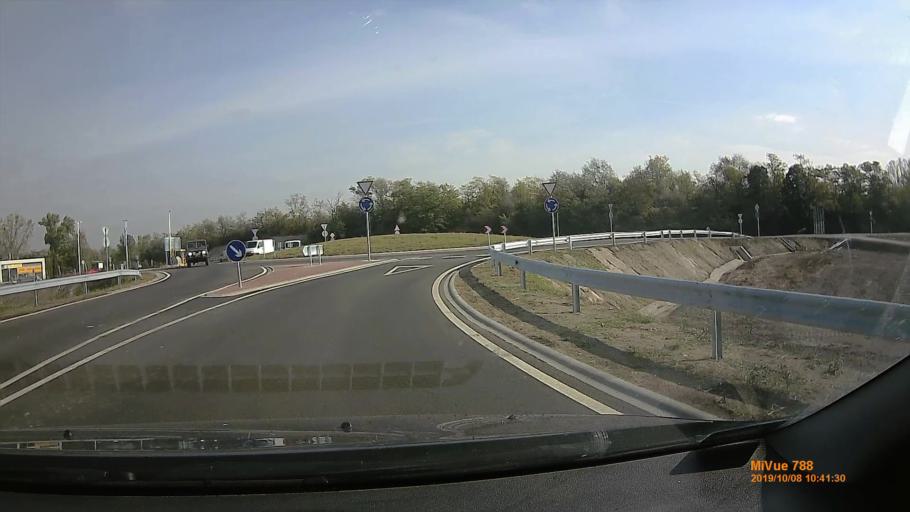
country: HU
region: Pest
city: God
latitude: 47.6656
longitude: 19.1312
